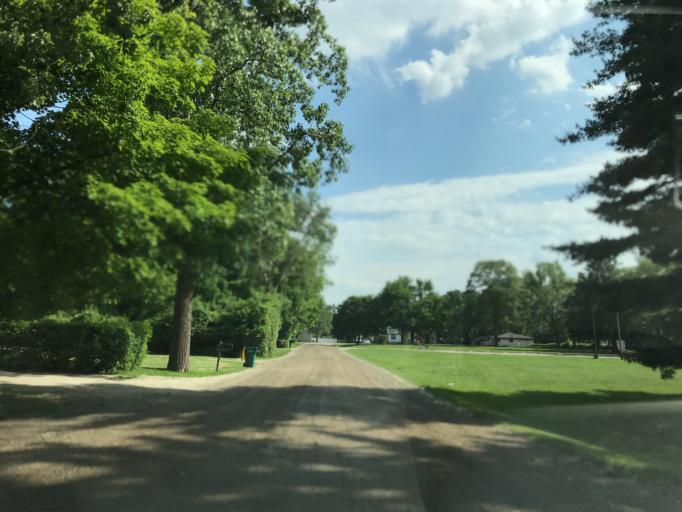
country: US
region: Michigan
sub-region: Oakland County
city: Farmington
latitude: 42.4549
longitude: -83.3296
